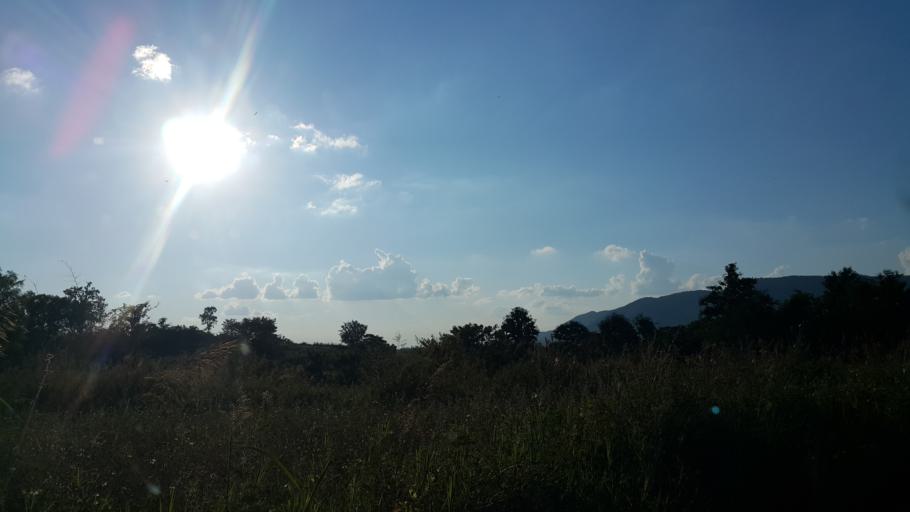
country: TH
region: Chiang Mai
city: Mae On
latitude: 18.7553
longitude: 99.2646
